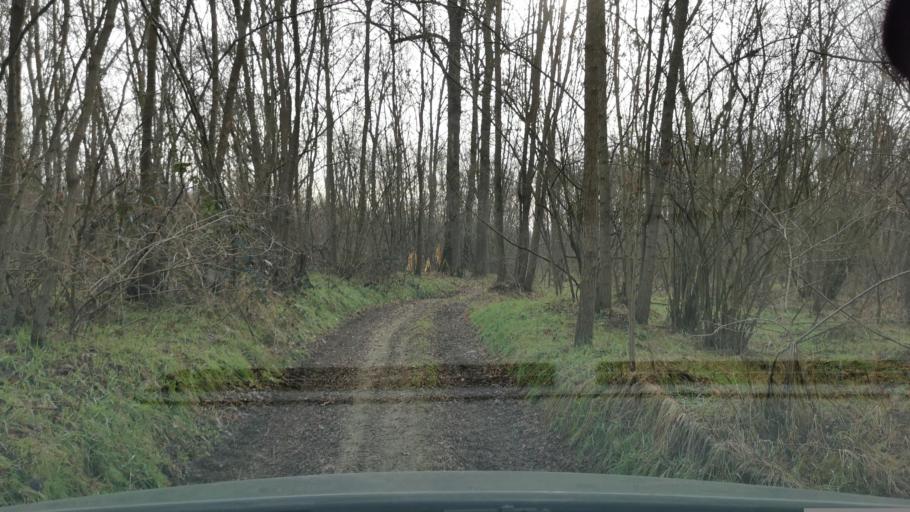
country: IT
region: Piedmont
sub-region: Provincia di Torino
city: San Benigno Canavese
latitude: 45.2551
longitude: 7.7950
